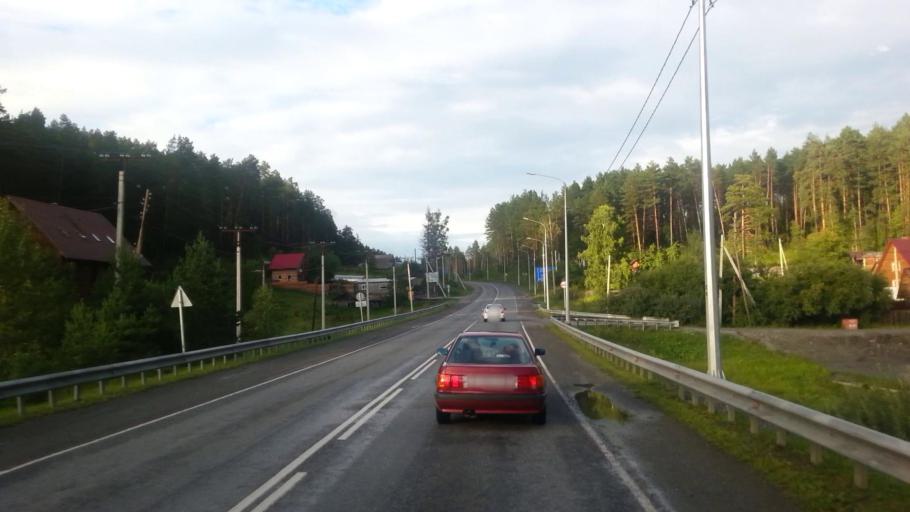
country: RU
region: Altay
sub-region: Mayminskiy Rayon
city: Manzherok
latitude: 51.8185
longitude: 85.7812
